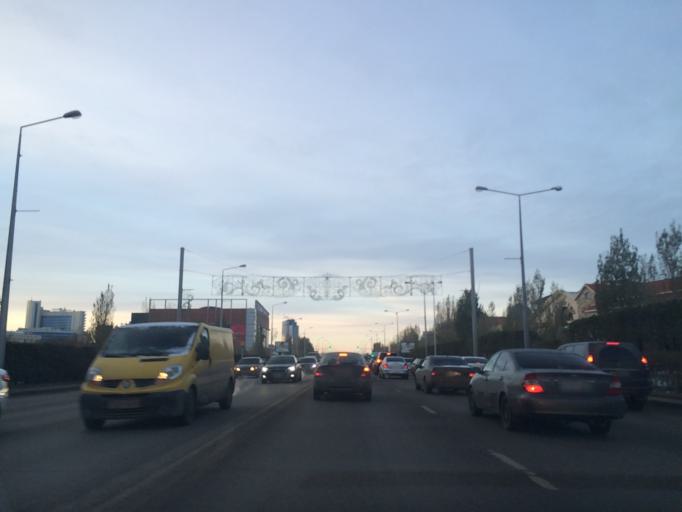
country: KZ
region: Astana Qalasy
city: Astana
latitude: 51.1418
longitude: 71.4104
